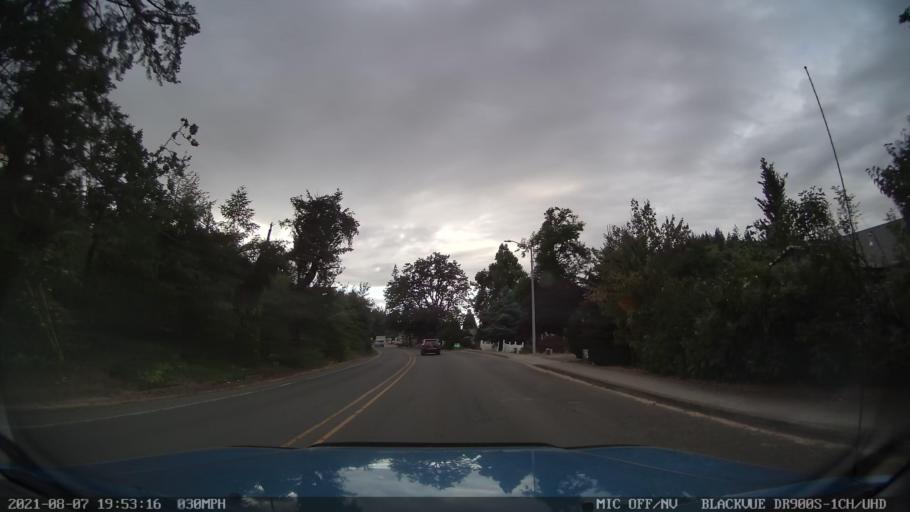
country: US
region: Oregon
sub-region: Marion County
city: Silverton
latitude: 44.9883
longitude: -122.7648
